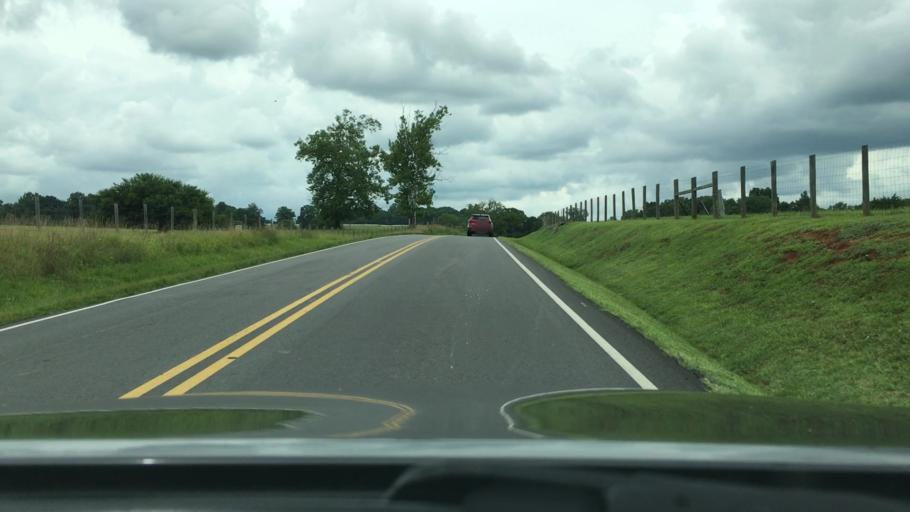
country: US
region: Virginia
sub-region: Orange County
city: Gordonsville
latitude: 38.1074
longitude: -78.2525
